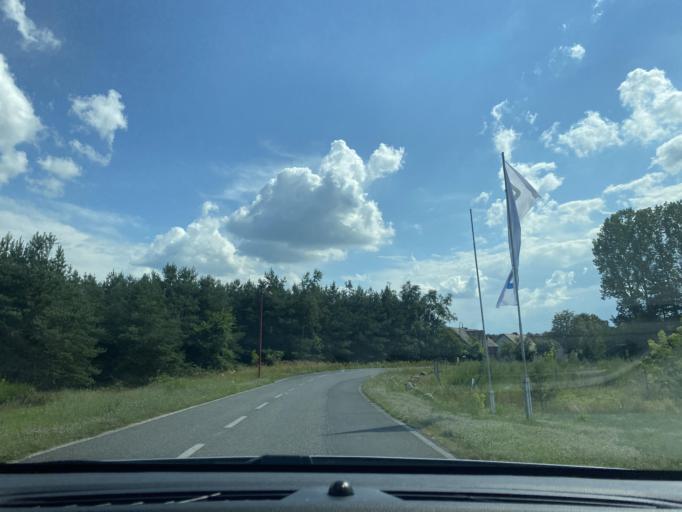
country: DE
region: Saxony
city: Boxberg
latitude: 51.4349
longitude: 14.6040
